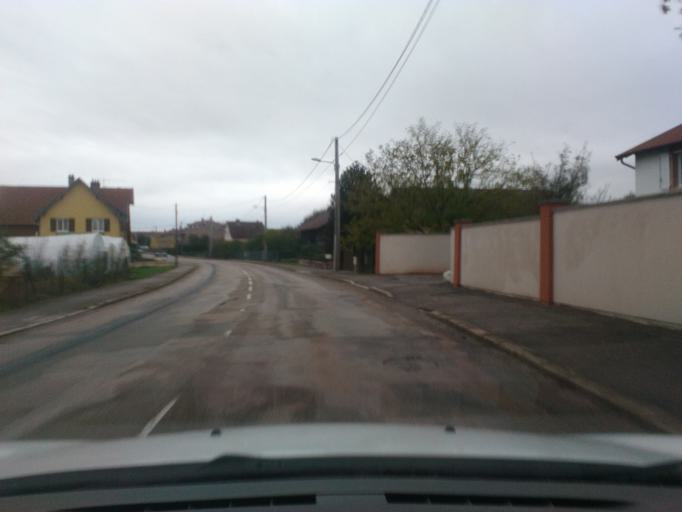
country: FR
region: Lorraine
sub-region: Departement des Vosges
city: Jeanmenil
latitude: 48.3353
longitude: 6.6942
